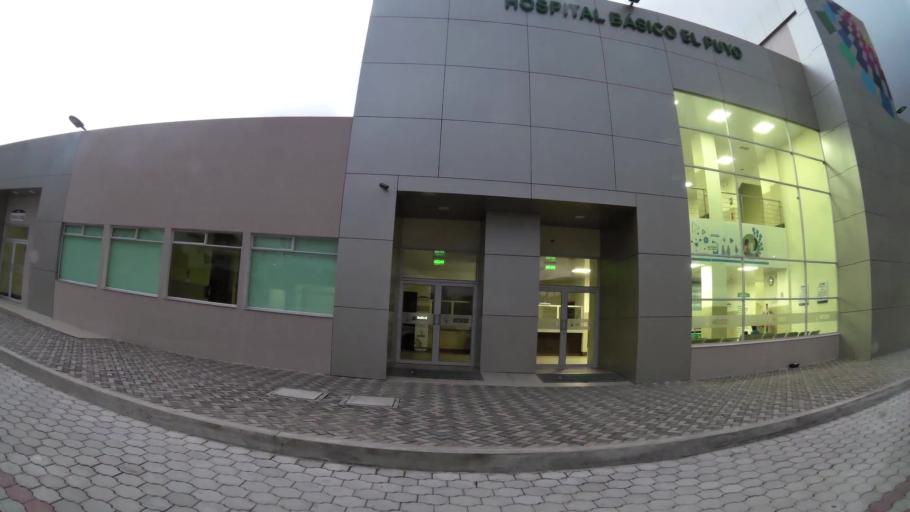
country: EC
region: Pastaza
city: Puyo
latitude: -1.4870
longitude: -78.0106
